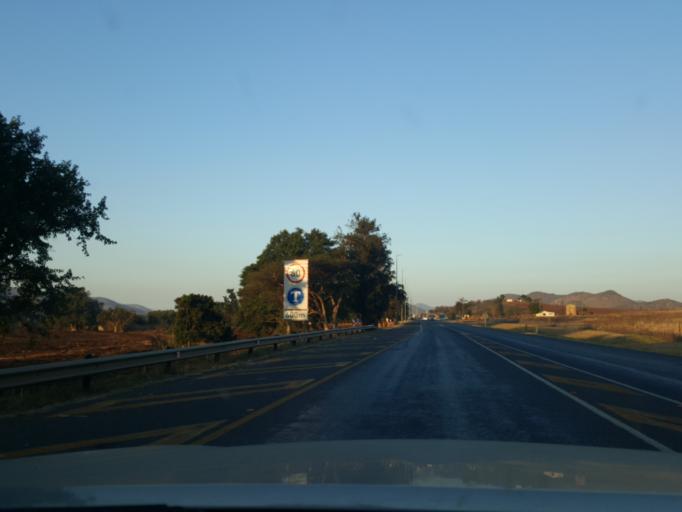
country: SZ
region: Hhohho
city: Ntfonjeni
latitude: -25.5366
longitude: 31.3361
